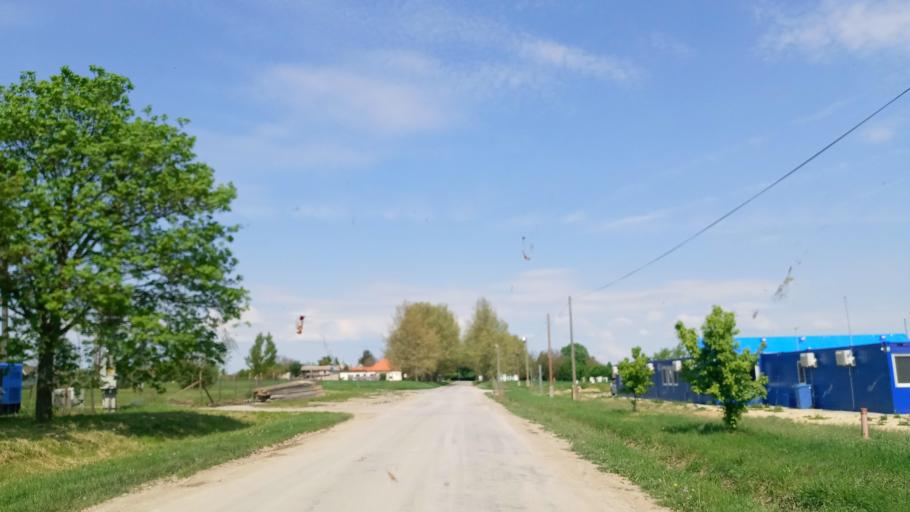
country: HU
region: Baranya
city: Boly
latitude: 45.9102
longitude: 18.5482
